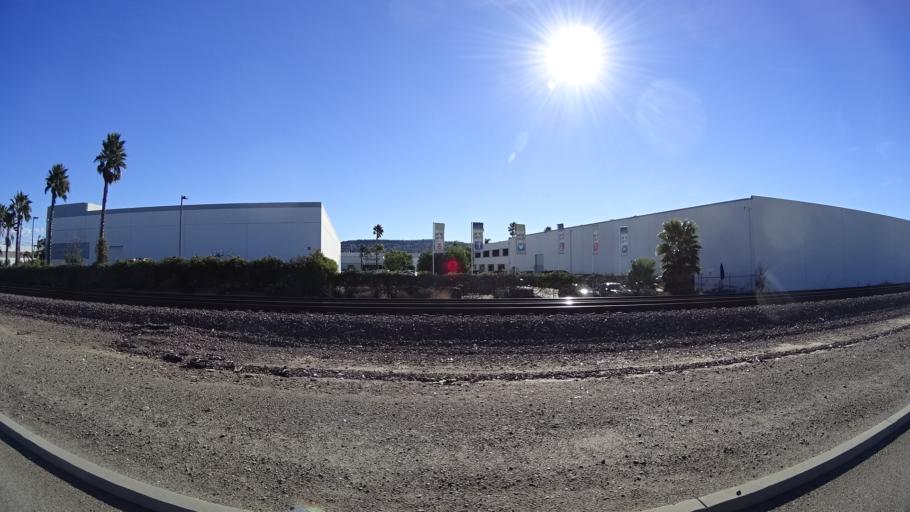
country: US
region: California
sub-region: Orange County
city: Yorba Linda
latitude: 33.8643
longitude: -117.8010
